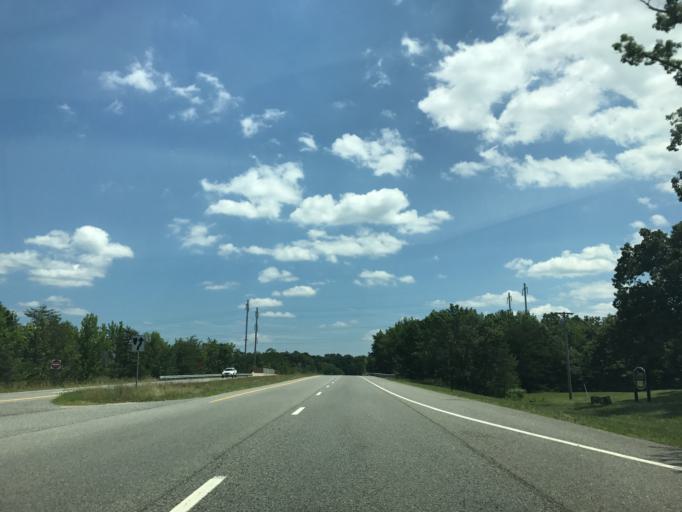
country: US
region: Maryland
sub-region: Prince George's County
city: Glenn Dale
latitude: 39.0184
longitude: -76.7674
